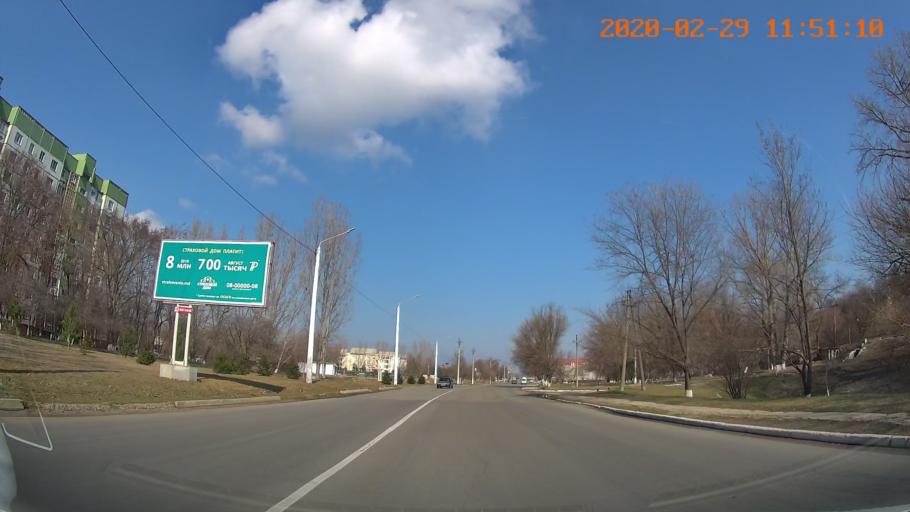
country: MD
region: Telenesti
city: Ribnita
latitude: 47.7633
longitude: 28.9897
